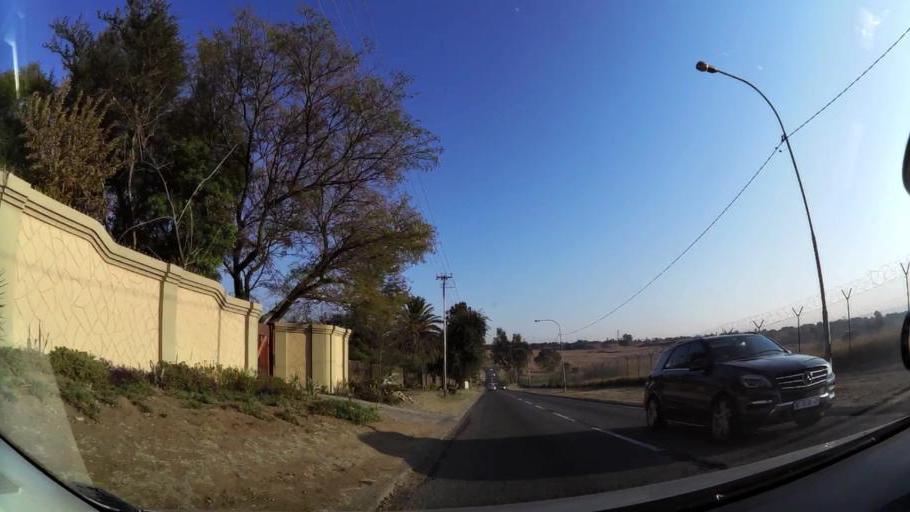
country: ZA
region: Gauteng
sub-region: City of Johannesburg Metropolitan Municipality
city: Modderfontein
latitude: -26.0732
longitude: 28.0977
